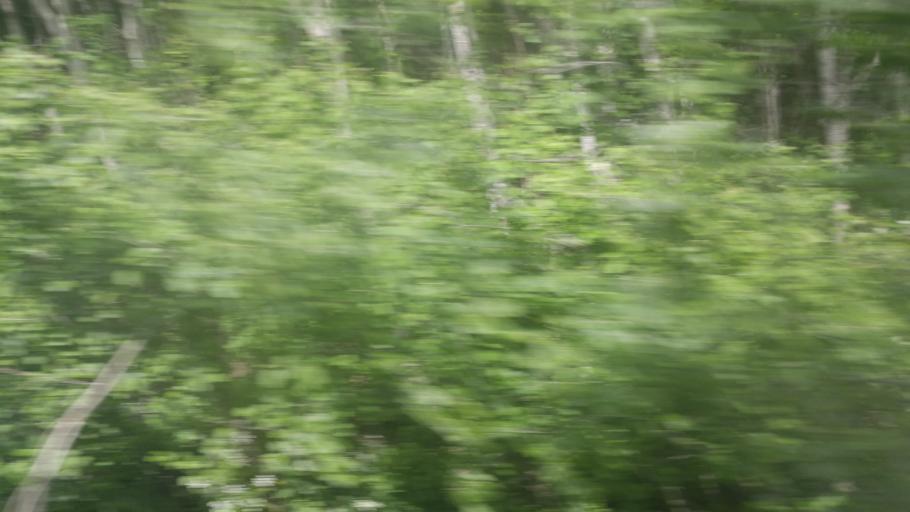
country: NO
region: Sor-Trondelag
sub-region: Klaebu
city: Klaebu
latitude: 62.9518
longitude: 10.6859
